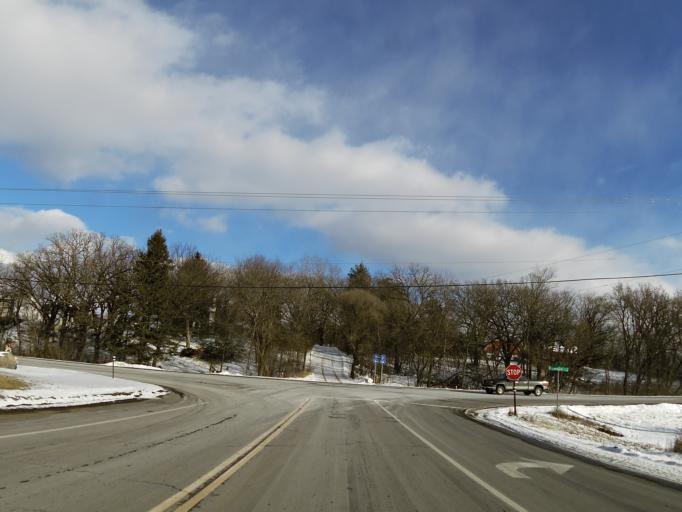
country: US
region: Minnesota
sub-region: Washington County
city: Oak Park Heights
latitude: 45.0178
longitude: -92.7980
